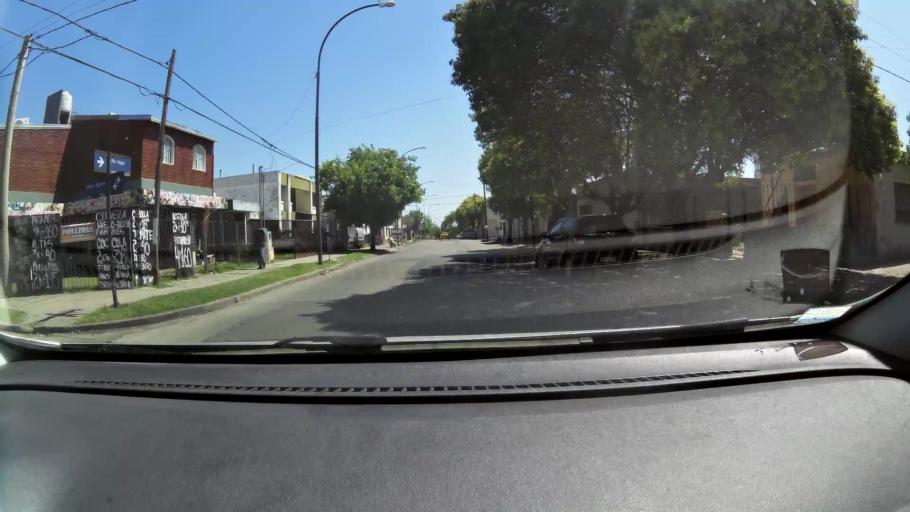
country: AR
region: Cordoba
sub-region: Departamento de Capital
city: Cordoba
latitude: -31.4241
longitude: -64.2095
